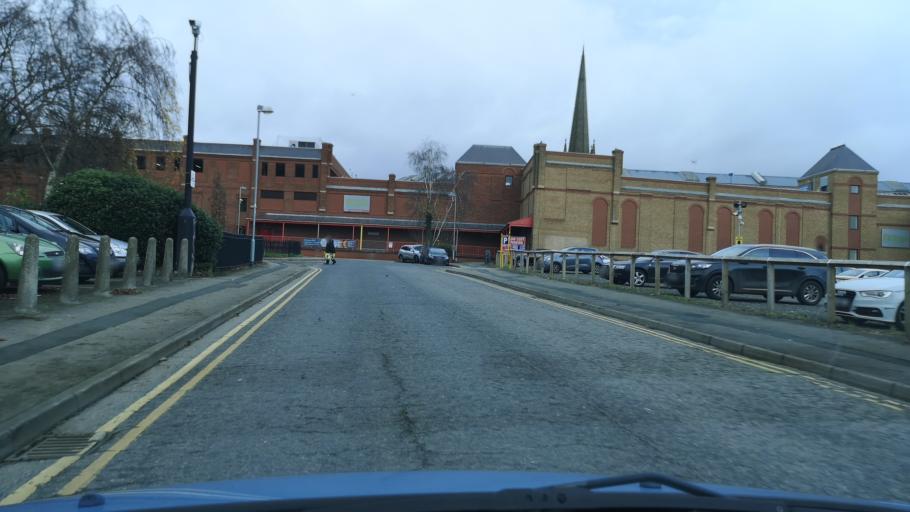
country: GB
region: England
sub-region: City and Borough of Wakefield
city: Wakefield
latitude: 53.6809
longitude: -1.4976
